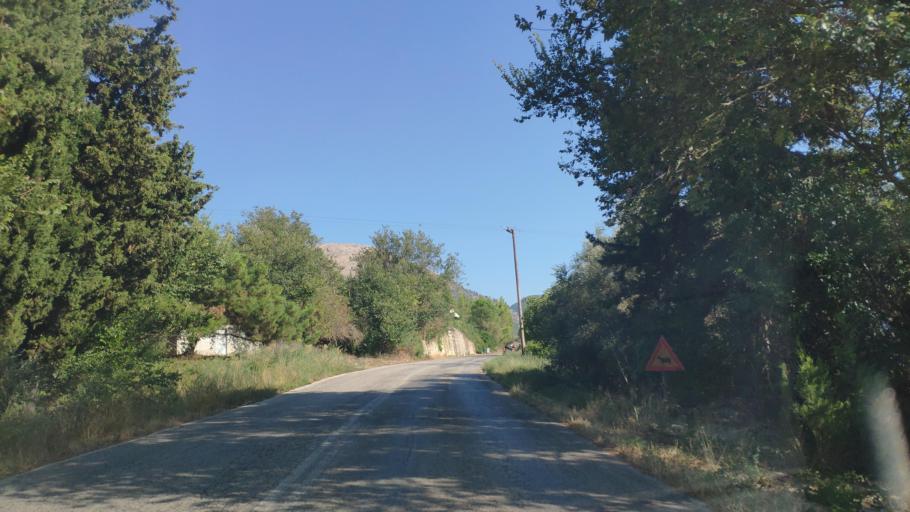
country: GR
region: Epirus
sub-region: Nomos Prevezis
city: Kanalaki
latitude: 39.2647
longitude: 20.6035
